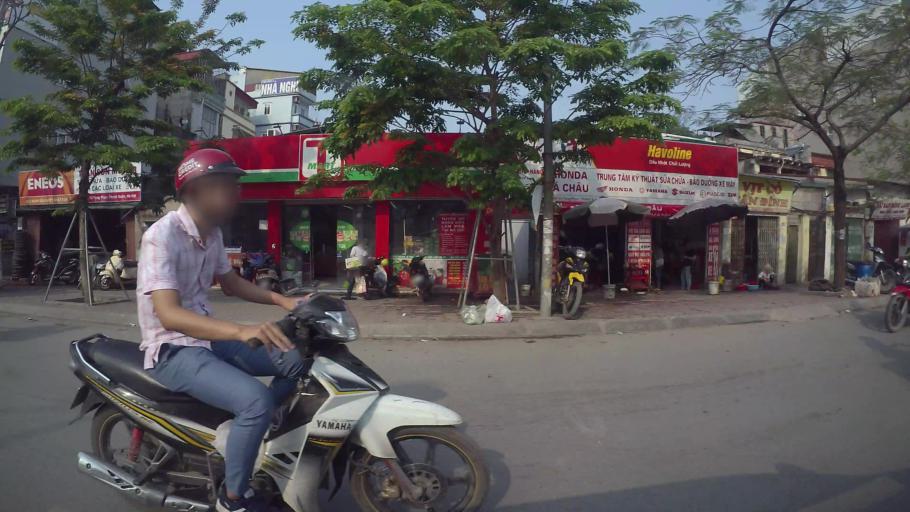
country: VN
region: Ha Noi
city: Thanh Xuan
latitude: 20.9865
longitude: 105.8140
